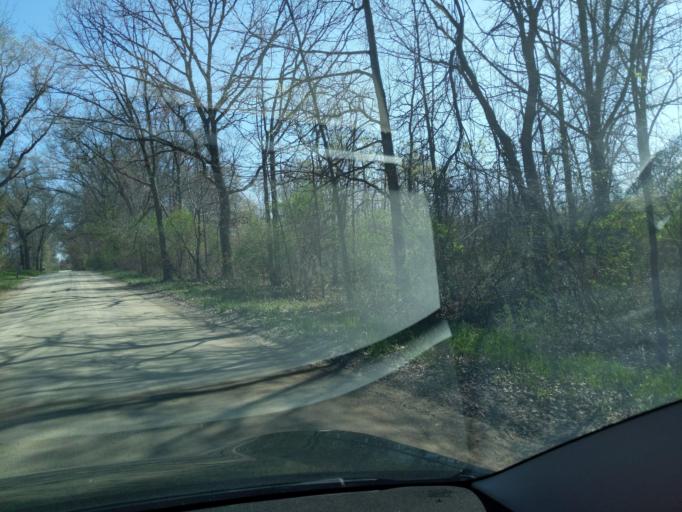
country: US
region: Michigan
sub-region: Ingham County
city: Stockbridge
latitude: 42.4284
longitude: -84.0828
